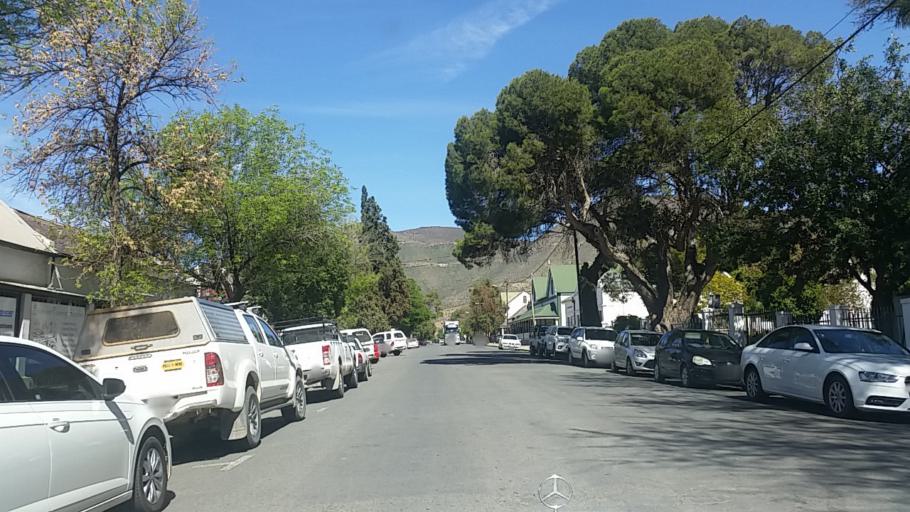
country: ZA
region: Eastern Cape
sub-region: Cacadu District Municipality
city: Graaff-Reinet
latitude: -32.2503
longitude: 24.5377
